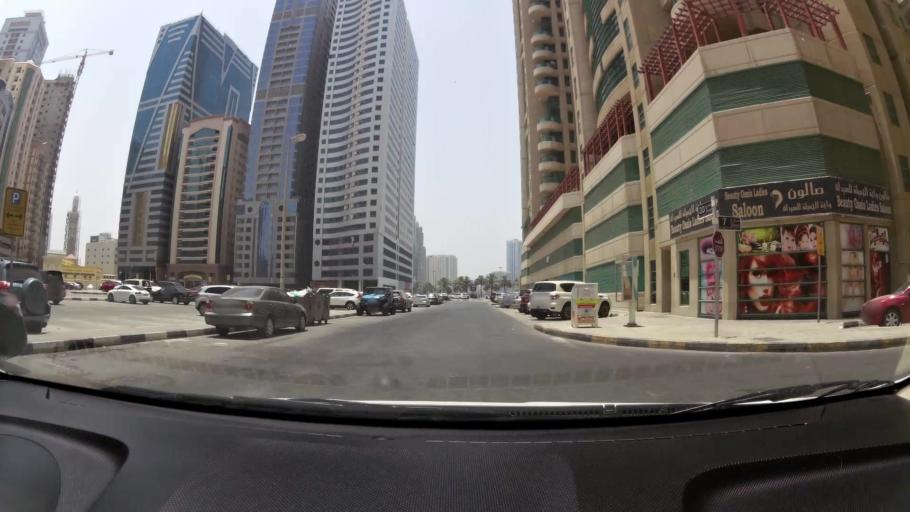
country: AE
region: Ash Shariqah
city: Sharjah
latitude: 25.3231
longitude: 55.3854
